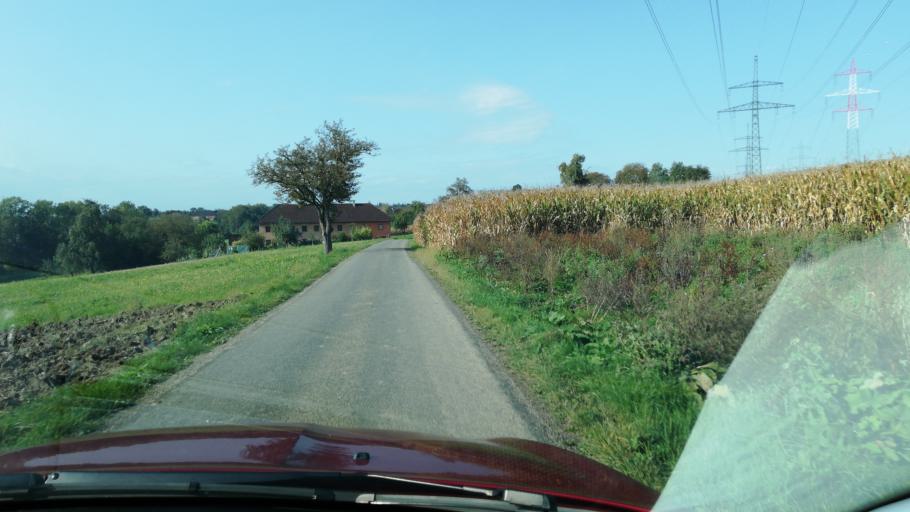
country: AT
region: Upper Austria
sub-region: Politischer Bezirk Kirchdorf an der Krems
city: Kremsmunster
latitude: 48.1001
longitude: 14.1738
